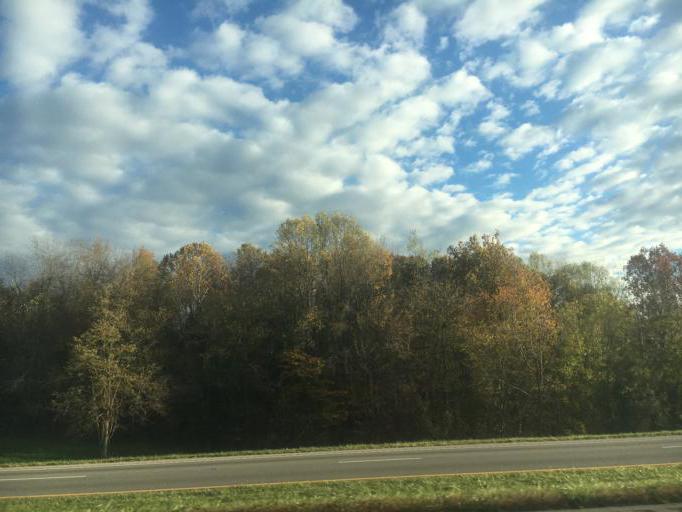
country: US
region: Virginia
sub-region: Washington County
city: Abingdon
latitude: 36.7094
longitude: -81.9459
